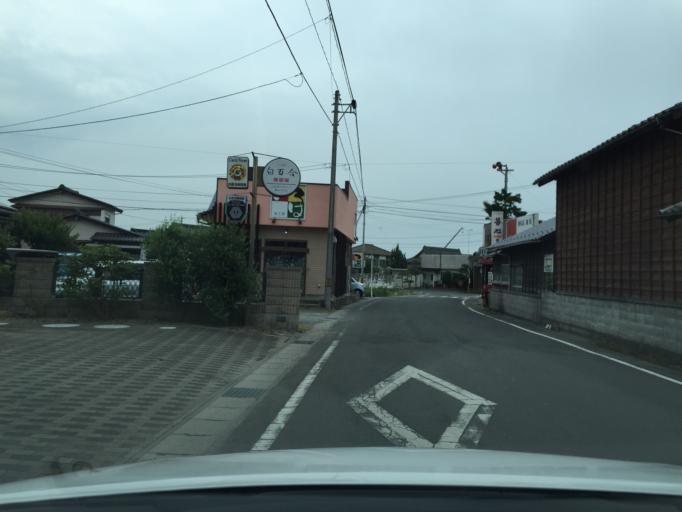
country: JP
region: Fukushima
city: Iwaki
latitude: 37.0120
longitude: 140.9716
